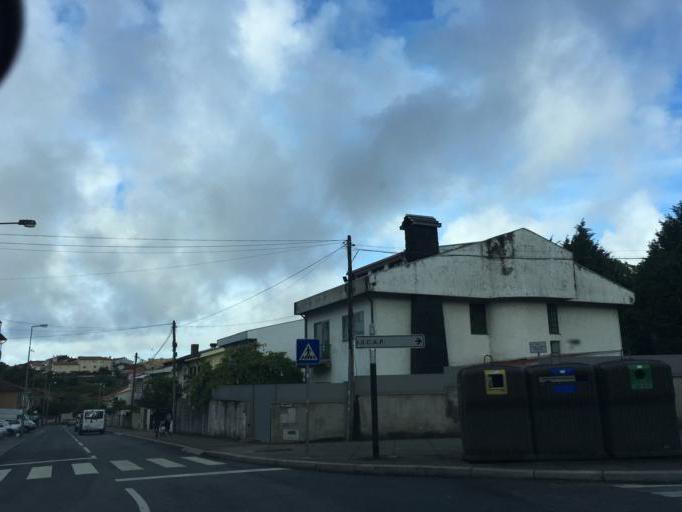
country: PT
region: Porto
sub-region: Matosinhos
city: Sao Mamede de Infesta
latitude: 41.1892
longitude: -8.5981
